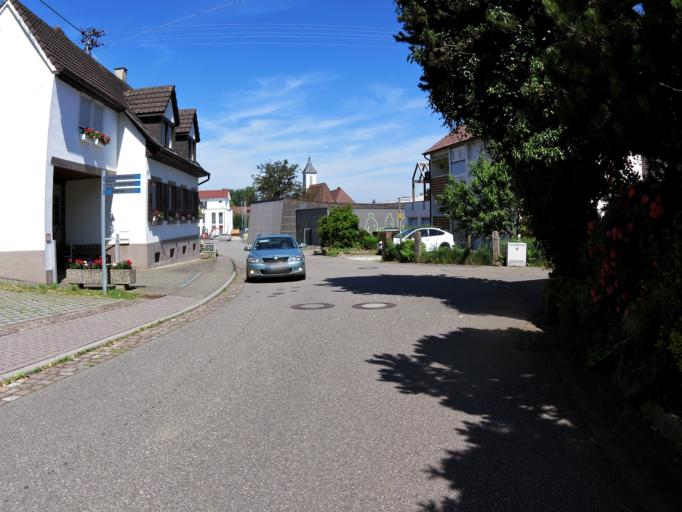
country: DE
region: Baden-Wuerttemberg
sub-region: Freiburg Region
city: Lahr
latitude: 48.3271
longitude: 7.8411
